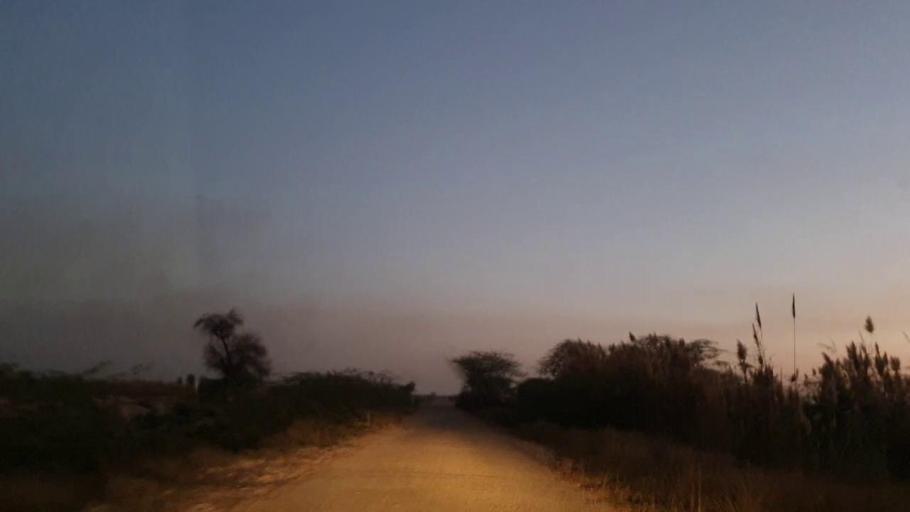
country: PK
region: Sindh
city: Nawabshah
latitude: 26.3377
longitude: 68.3722
